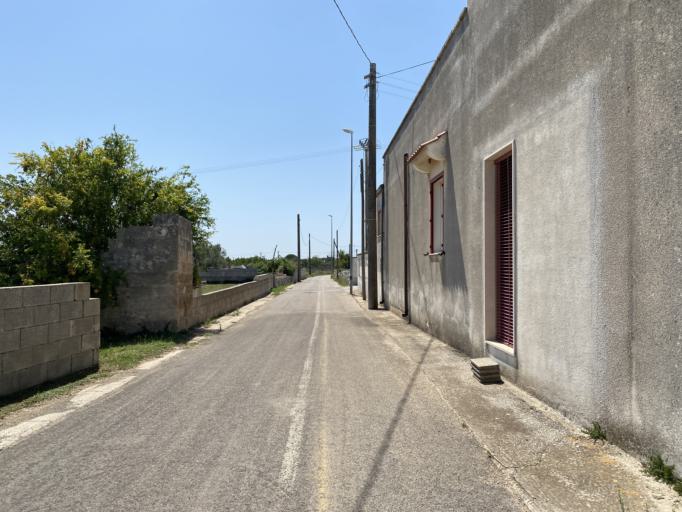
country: IT
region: Apulia
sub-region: Provincia di Lecce
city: Giuggianello
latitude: 40.0995
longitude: 18.3644
